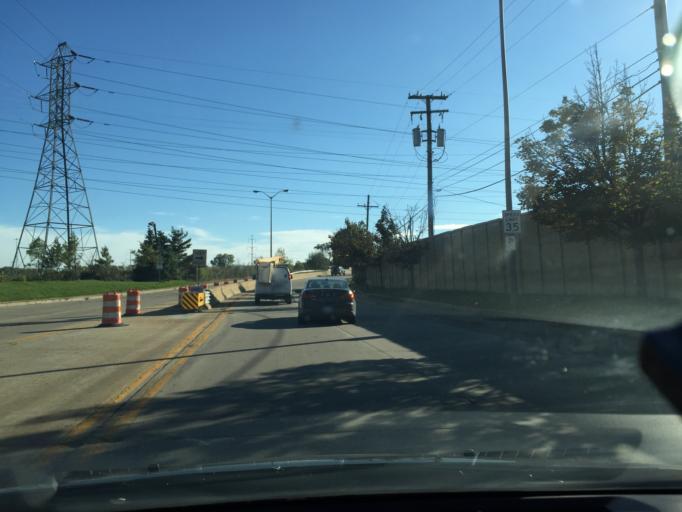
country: US
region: Michigan
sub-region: Oakland County
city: Pontiac
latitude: 42.6194
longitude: -83.2683
